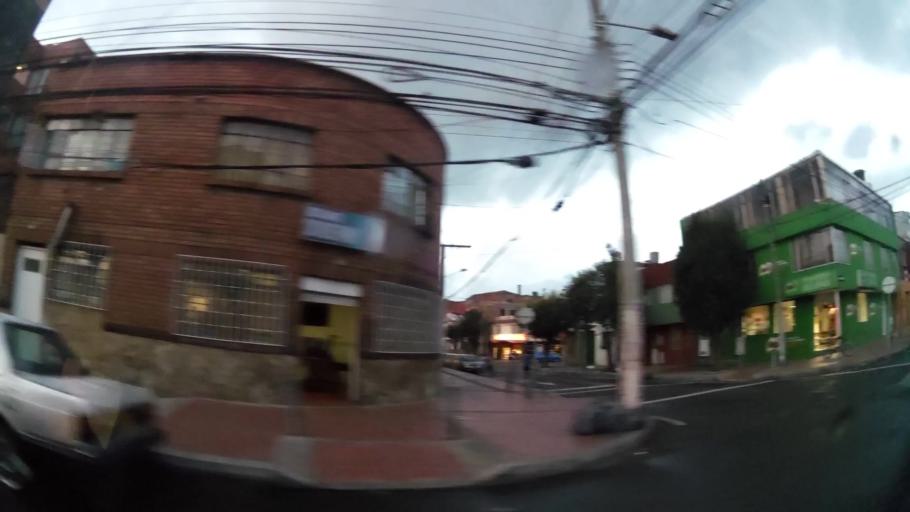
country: CO
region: Bogota D.C.
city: Barrio San Luis
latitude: 4.6753
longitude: -74.0732
